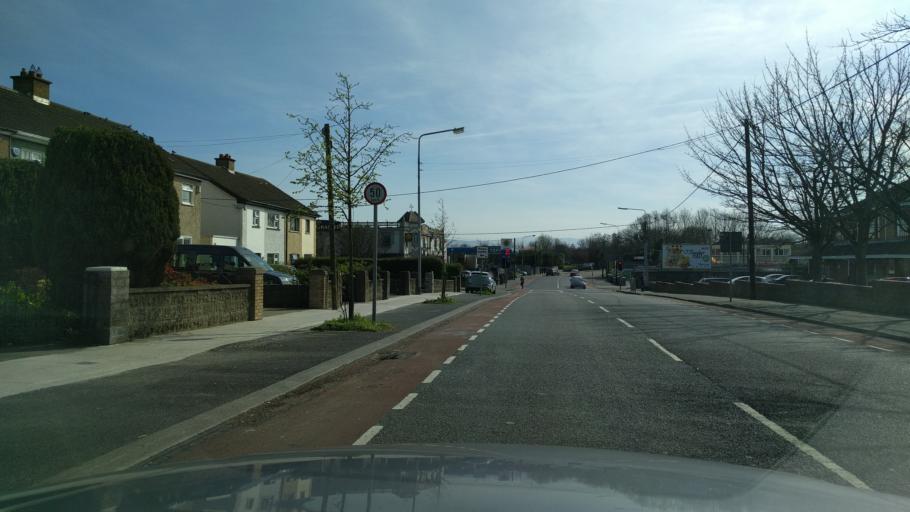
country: IE
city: Palmerstown
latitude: 53.3513
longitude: -6.3779
